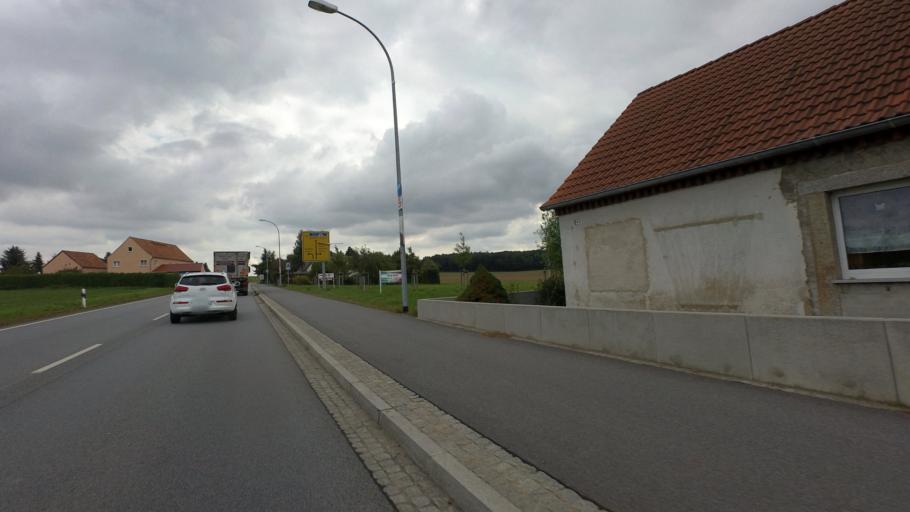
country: DE
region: Saxony
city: Radibor
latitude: 51.2379
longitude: 14.3692
